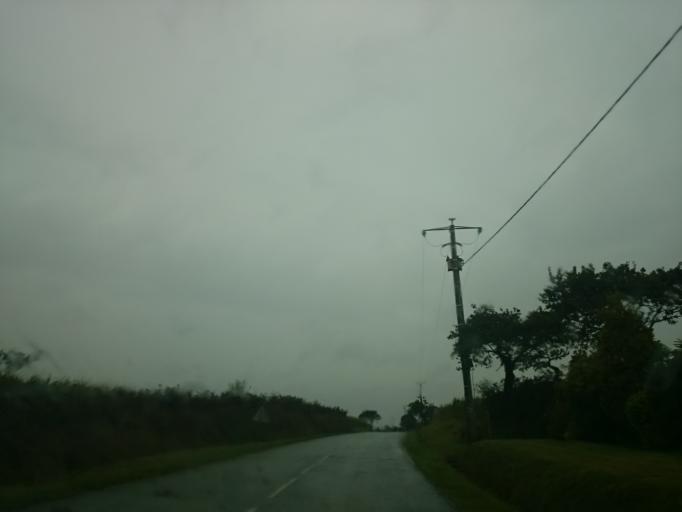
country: FR
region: Brittany
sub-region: Departement du Finistere
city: Kernilis
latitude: 48.5443
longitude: -4.4131
